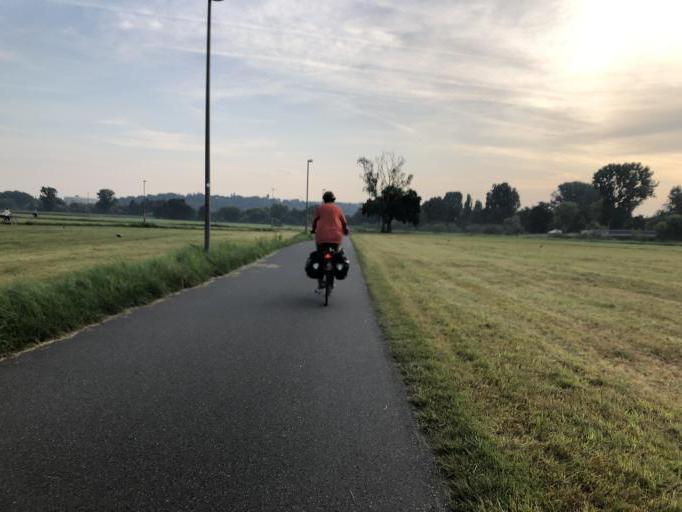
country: DE
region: Bavaria
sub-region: Regierungsbezirk Mittelfranken
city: Erlangen
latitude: 49.5960
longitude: 10.9910
